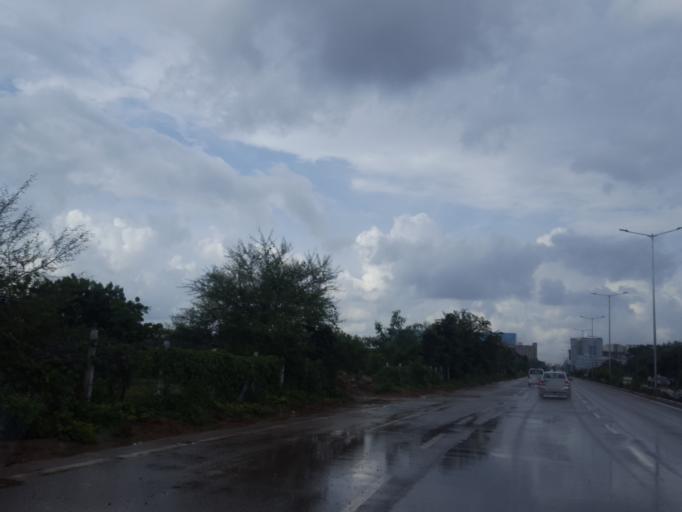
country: IN
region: Telangana
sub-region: Medak
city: Serilingampalle
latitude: 17.4104
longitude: 78.3307
